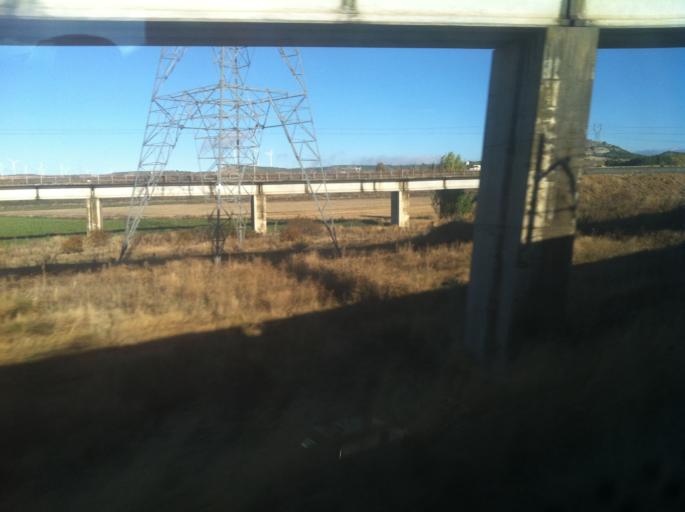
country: ES
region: Castille and Leon
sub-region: Provincia de Palencia
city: Soto de Cerrato
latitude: 41.9673
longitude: -4.4383
